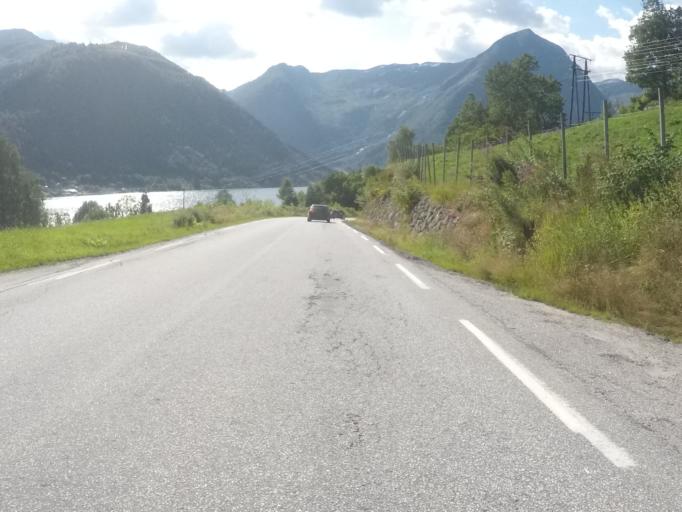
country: NO
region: Sogn og Fjordane
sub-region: Balestrand
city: Balestrand
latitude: 61.2155
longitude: 6.5418
